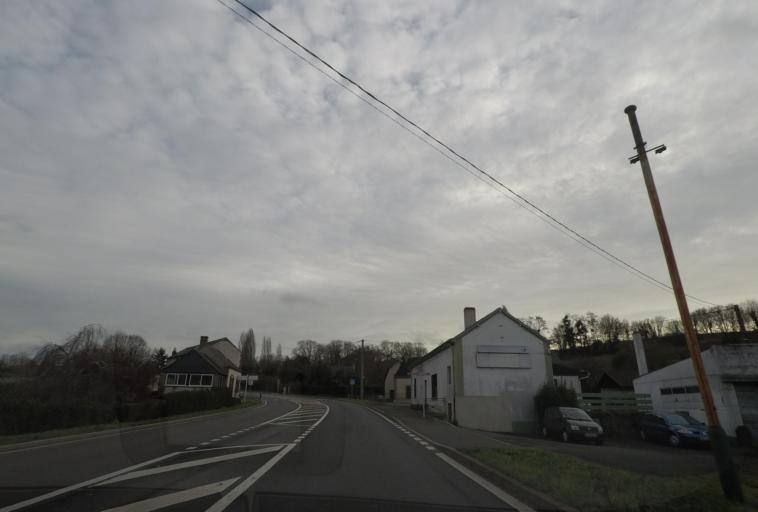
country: FR
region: Centre
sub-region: Departement du Loir-et-Cher
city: Sarge-sur-Braye
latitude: 47.9098
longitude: 0.8469
